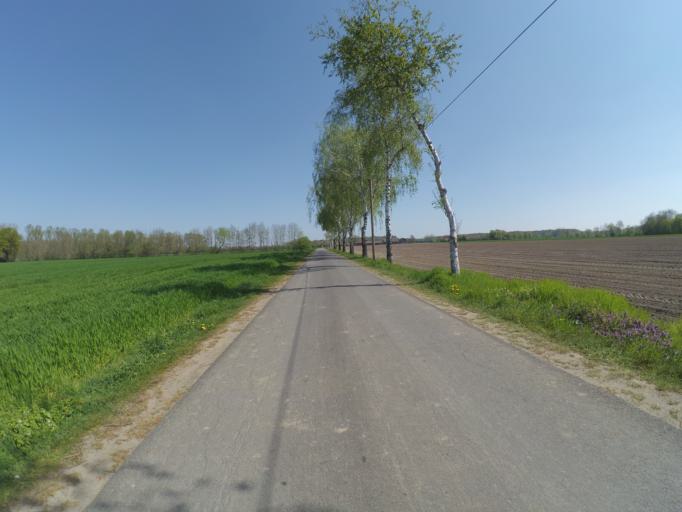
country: DE
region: North Rhine-Westphalia
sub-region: Regierungsbezirk Munster
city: Nordkirchen
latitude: 51.7464
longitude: 7.5302
